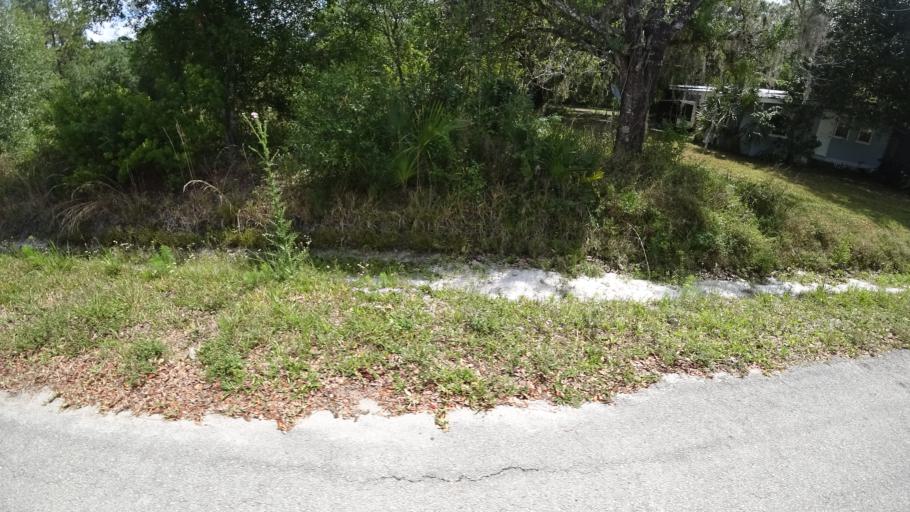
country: US
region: Florida
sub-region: Sarasota County
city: Lake Sarasota
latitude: 27.3515
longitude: -82.1605
